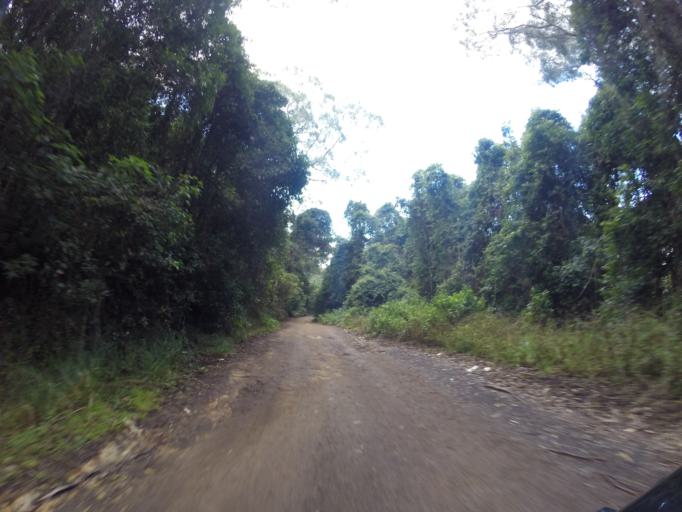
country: AU
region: New South Wales
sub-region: Wollongong
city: Cordeaux Heights
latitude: -34.4380
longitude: 150.7889
